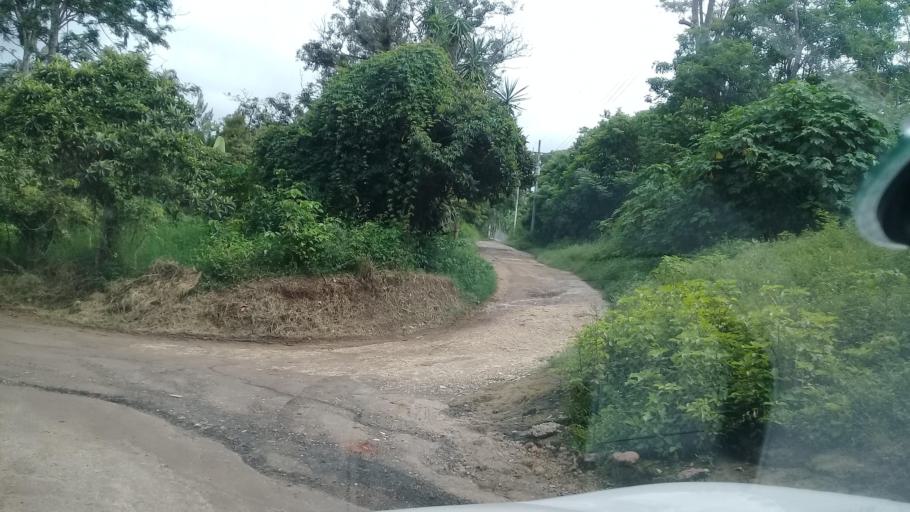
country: MX
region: Veracruz
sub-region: Emiliano Zapata
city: Jacarandas
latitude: 19.4807
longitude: -96.8526
